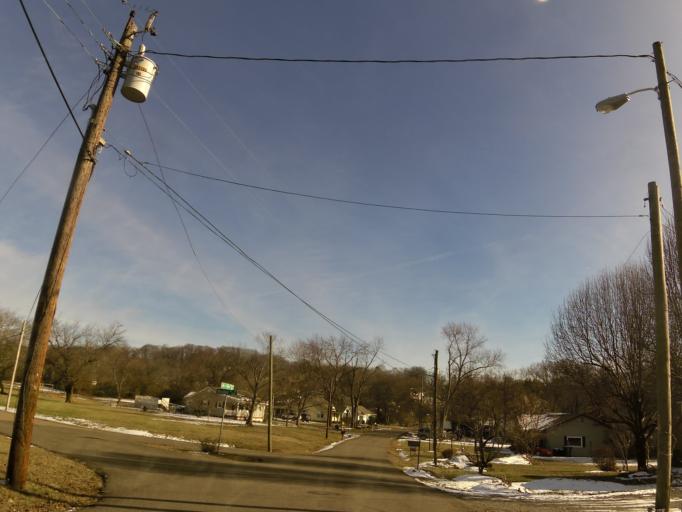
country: US
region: Tennessee
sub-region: Knox County
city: Knoxville
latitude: 35.9706
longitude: -83.9777
